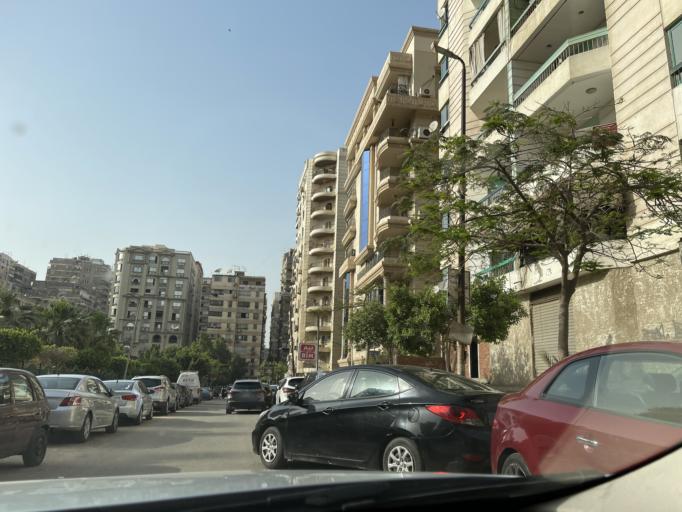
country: EG
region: Muhafazat al Qahirah
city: Cairo
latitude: 30.0658
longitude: 31.3507
